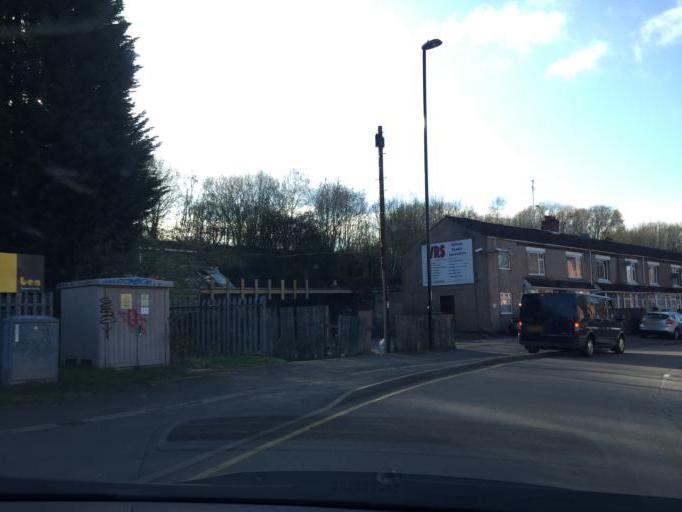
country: GB
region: England
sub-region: Coventry
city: Coventry
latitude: 52.3978
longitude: -1.4878
